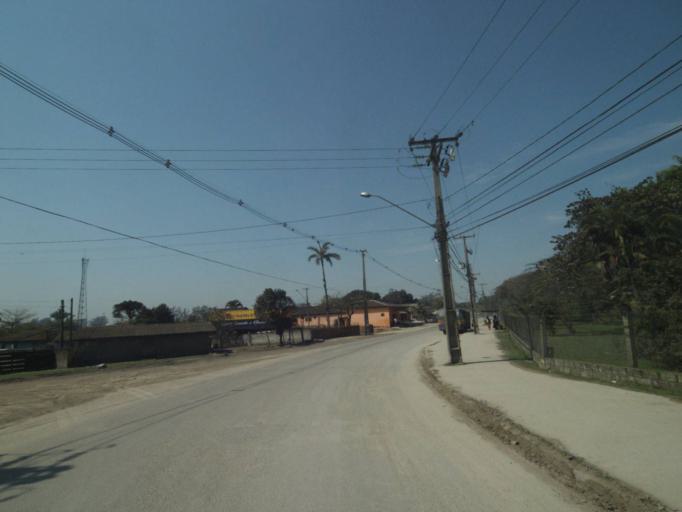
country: BR
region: Parana
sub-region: Paranagua
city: Paranagua
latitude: -25.5456
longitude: -48.5695
